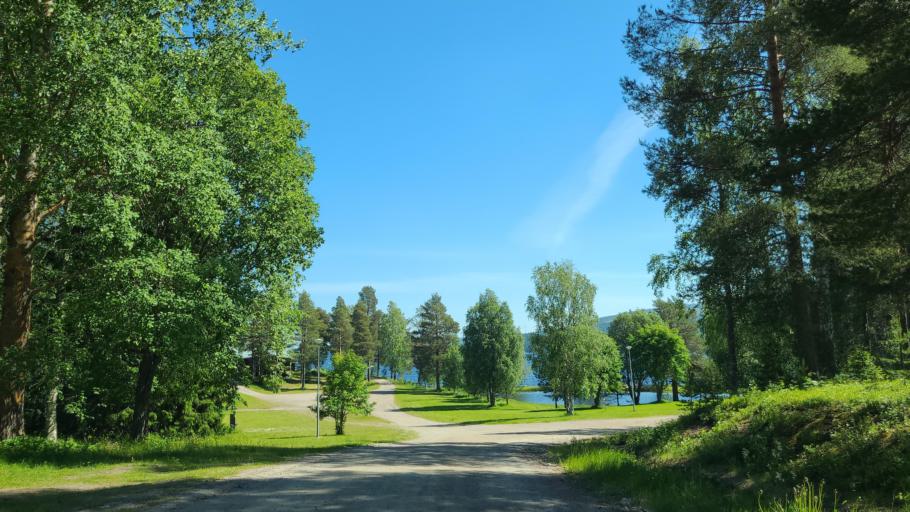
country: SE
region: Vaesterbotten
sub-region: Bjurholms Kommun
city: Bjurholm
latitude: 63.6896
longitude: 18.8657
